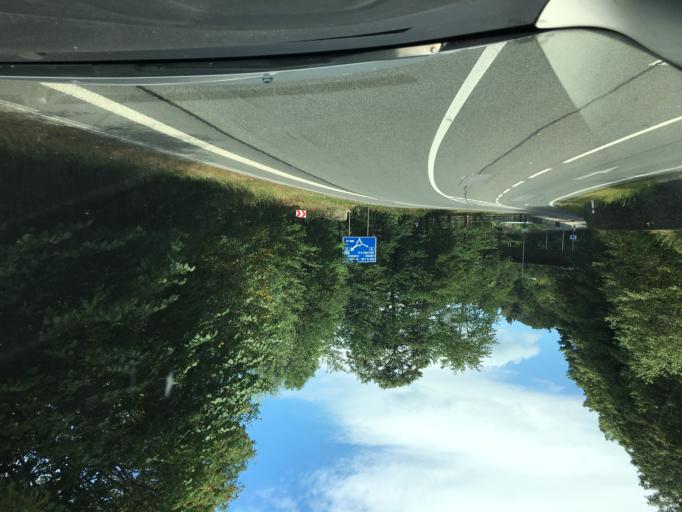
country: CZ
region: Liberecky
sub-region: Okres Jablonec nad Nisou
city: Tanvald
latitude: 50.7324
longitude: 15.3132
